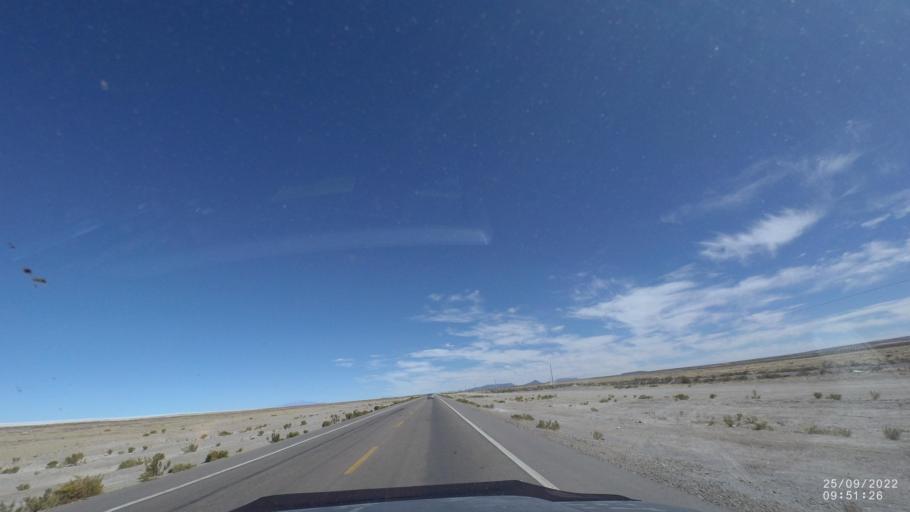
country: BO
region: Potosi
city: Colchani
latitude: -20.3773
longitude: -66.8880
